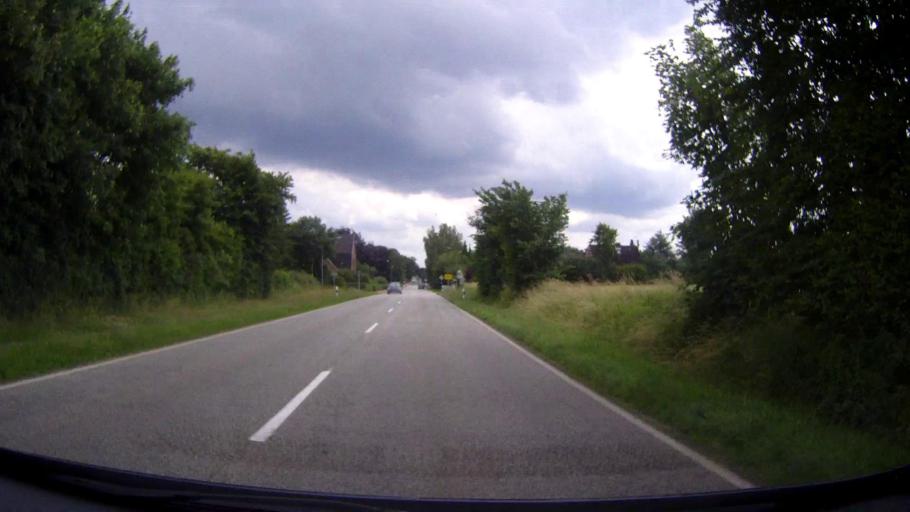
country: DE
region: Schleswig-Holstein
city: Schenefeld
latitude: 54.0534
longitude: 9.4789
